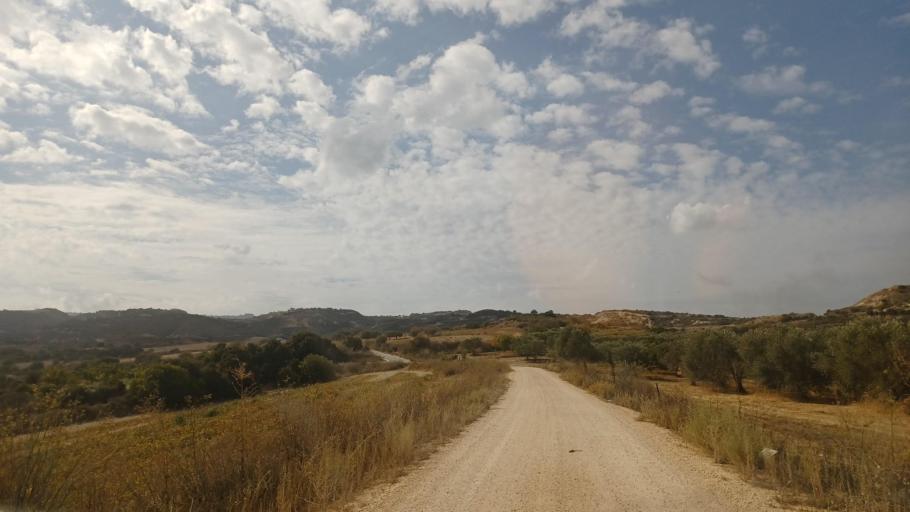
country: CY
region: Pafos
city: Polis
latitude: 35.0169
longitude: 32.4148
